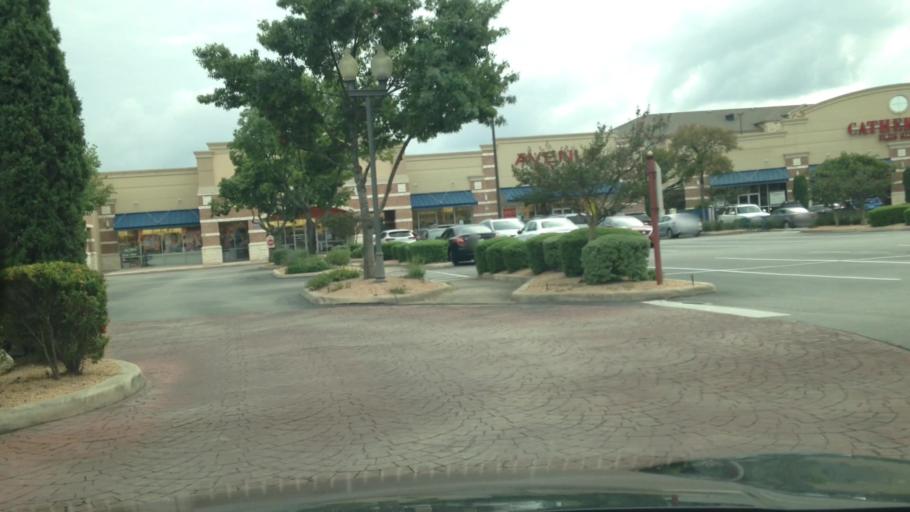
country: US
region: Texas
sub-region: Bexar County
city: Hollywood Park
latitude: 29.6072
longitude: -98.4649
